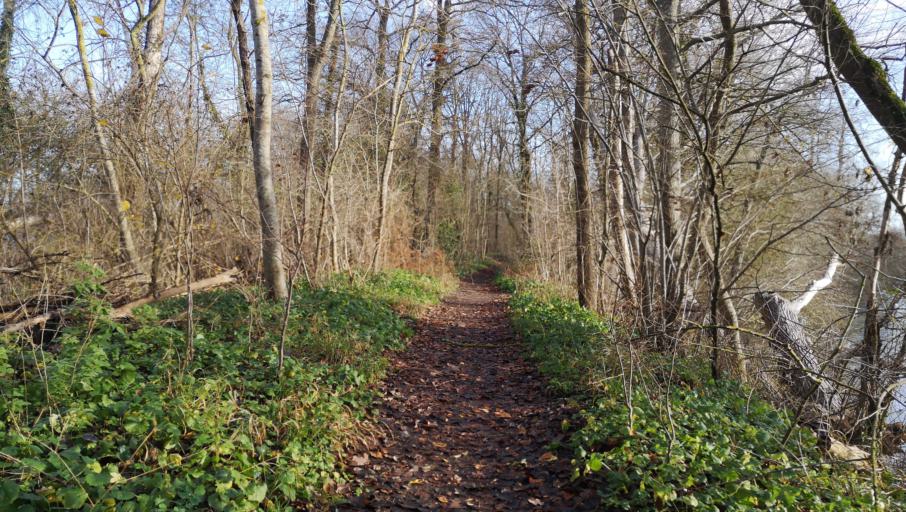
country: FR
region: Centre
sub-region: Departement du Loiret
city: Mareau-aux-Pres
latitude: 47.8638
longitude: 1.8038
